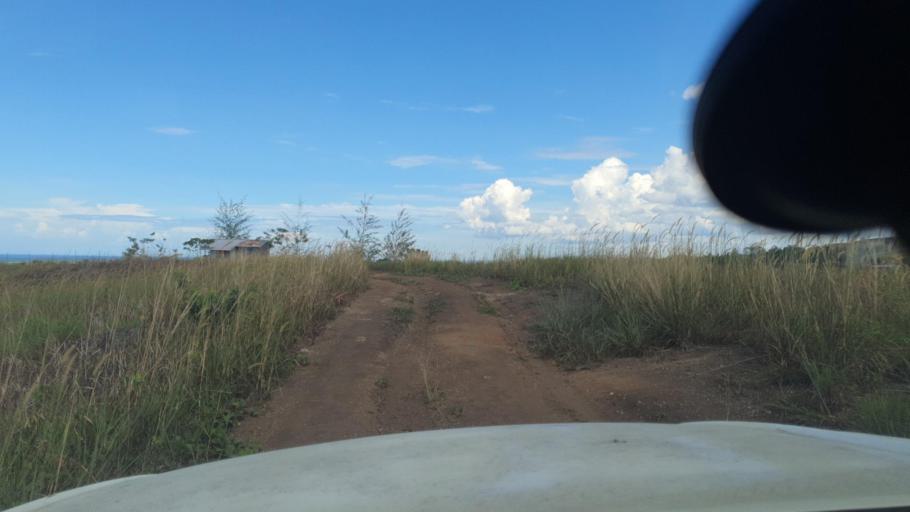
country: SB
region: Guadalcanal
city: Honiara
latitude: -9.4530
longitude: 159.9692
